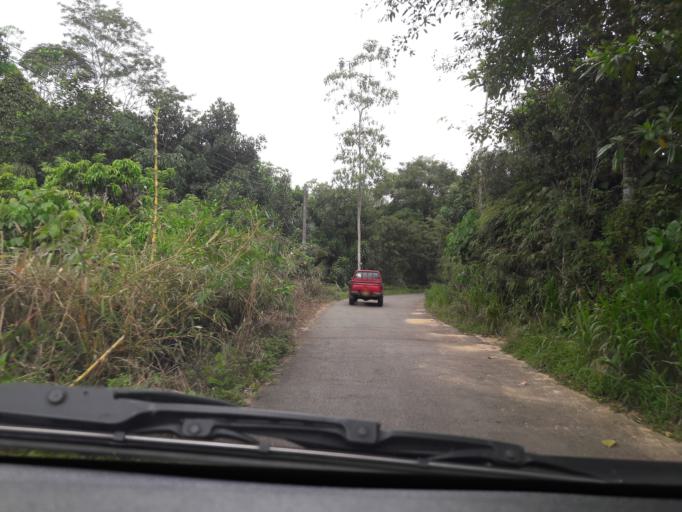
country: LK
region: Southern
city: Galle
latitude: 6.1876
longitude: 80.3045
